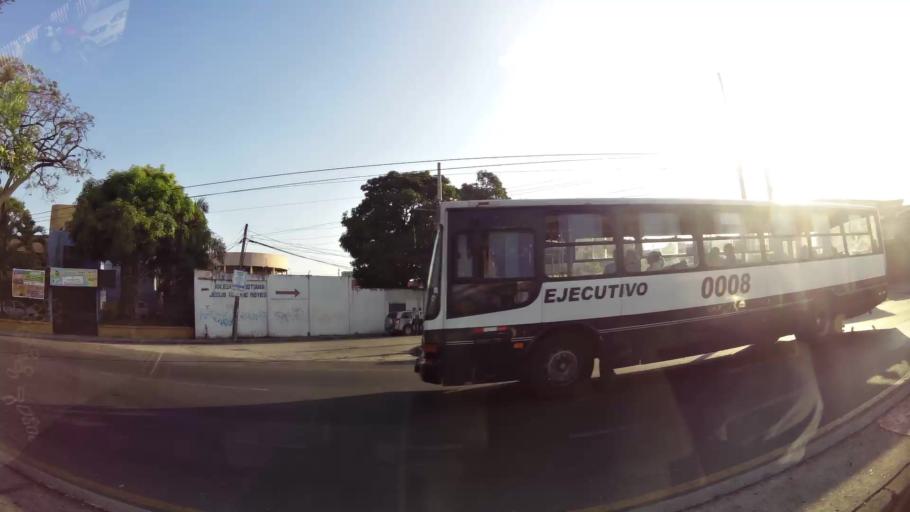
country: EC
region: Guayas
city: Guayaquil
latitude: -2.1787
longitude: -79.8974
